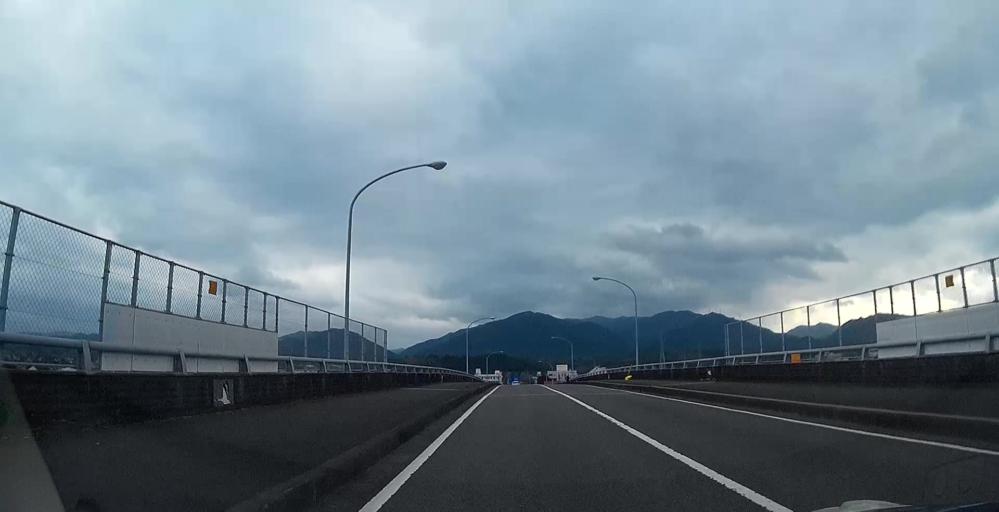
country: JP
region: Kagoshima
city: Izumi
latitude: 32.0779
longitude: 130.3461
